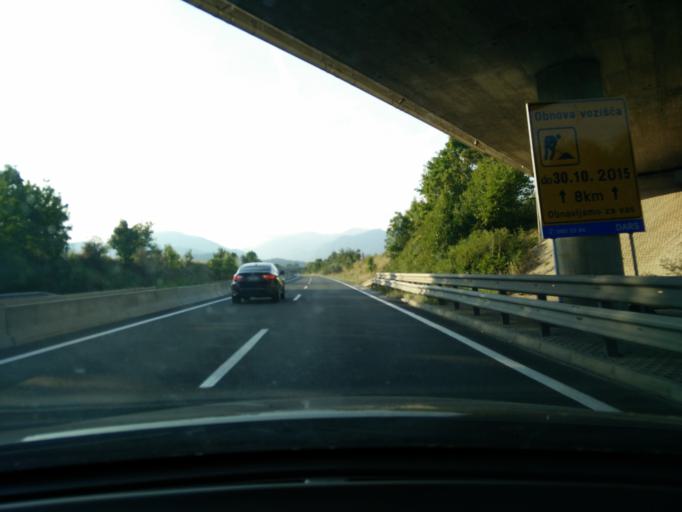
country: SI
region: Radovljica
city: Lesce
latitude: 46.3804
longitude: 14.1496
